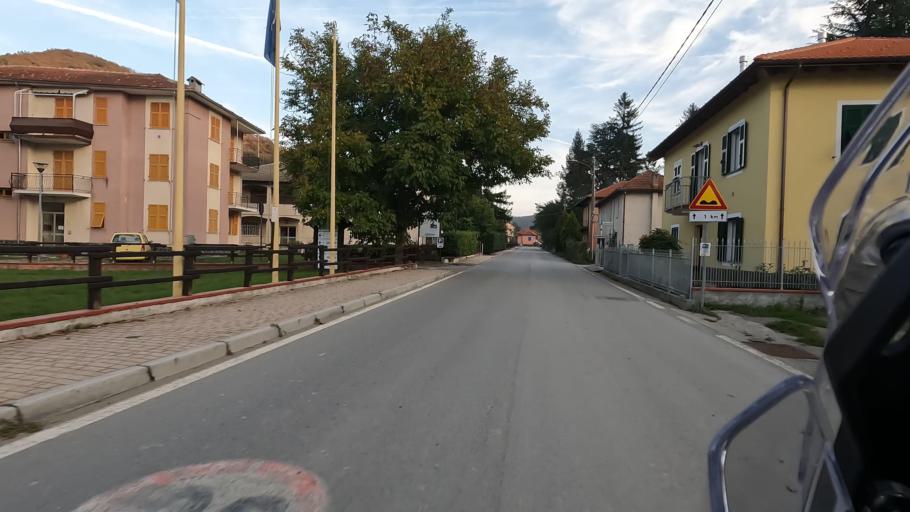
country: IT
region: Liguria
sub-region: Provincia di Savona
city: Pontinvrea
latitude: 44.4441
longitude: 8.4354
